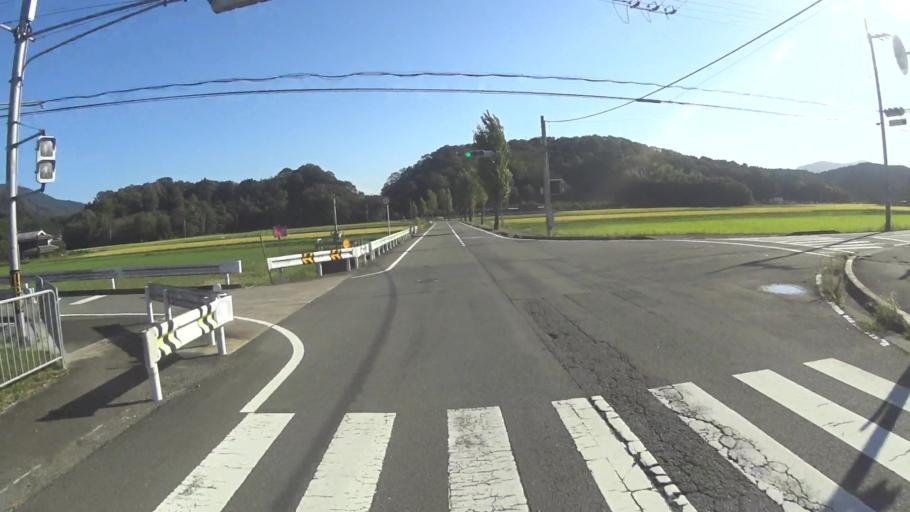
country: JP
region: Kyoto
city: Kameoka
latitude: 35.0749
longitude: 135.5660
